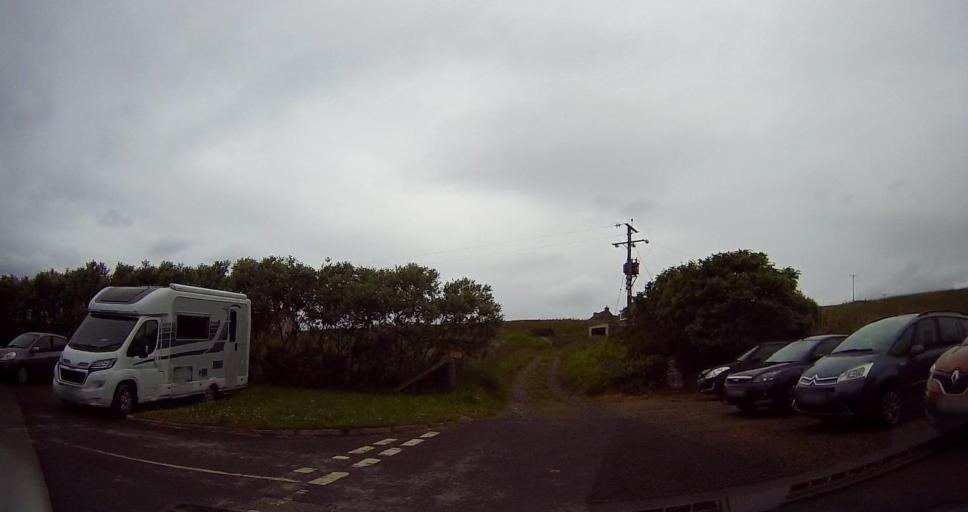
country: GB
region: Scotland
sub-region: Orkney Islands
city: Stromness
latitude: 59.0695
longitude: -3.3094
